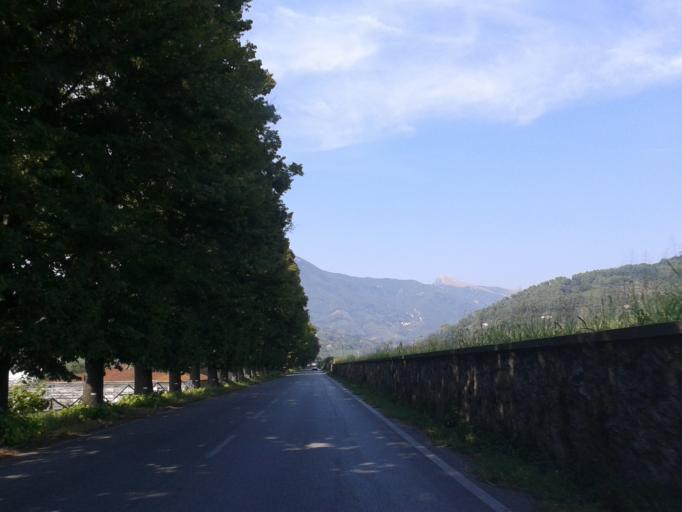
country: IT
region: Tuscany
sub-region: Provincia di Lucca
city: Piano di Mommio
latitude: 43.9159
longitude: 10.2648
